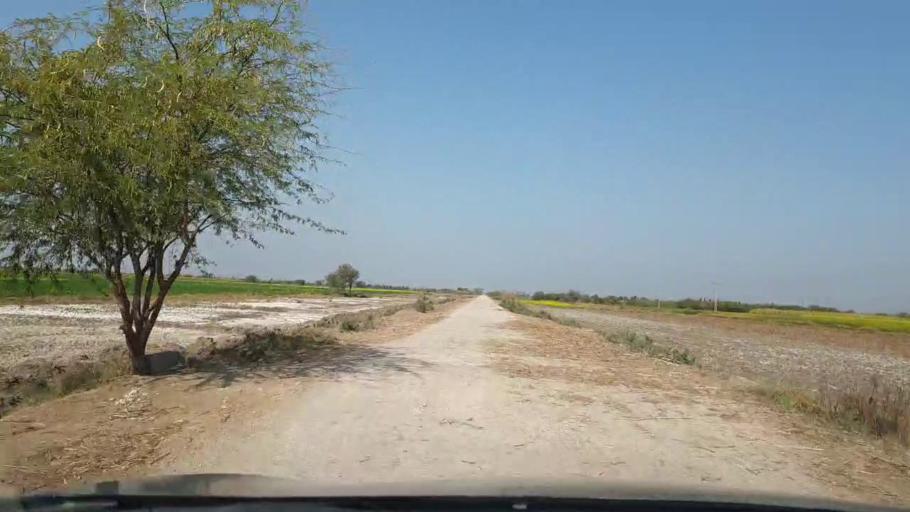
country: PK
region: Sindh
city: Mirpur Khas
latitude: 25.6016
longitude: 68.8897
